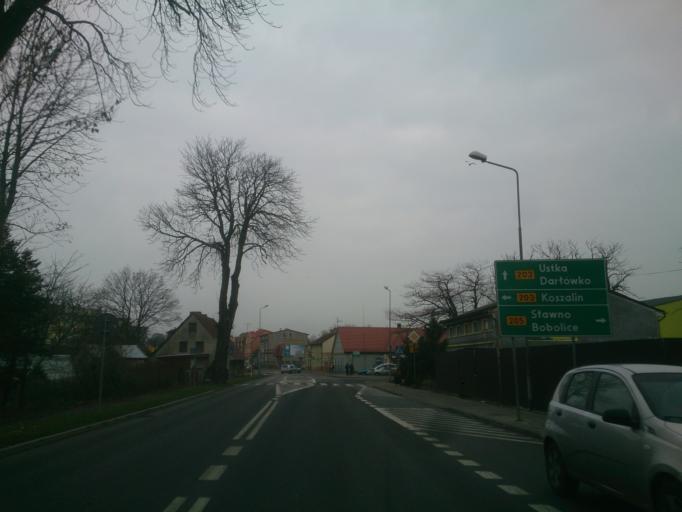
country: PL
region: West Pomeranian Voivodeship
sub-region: Powiat slawienski
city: Darlowo
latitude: 54.4147
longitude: 16.4107
